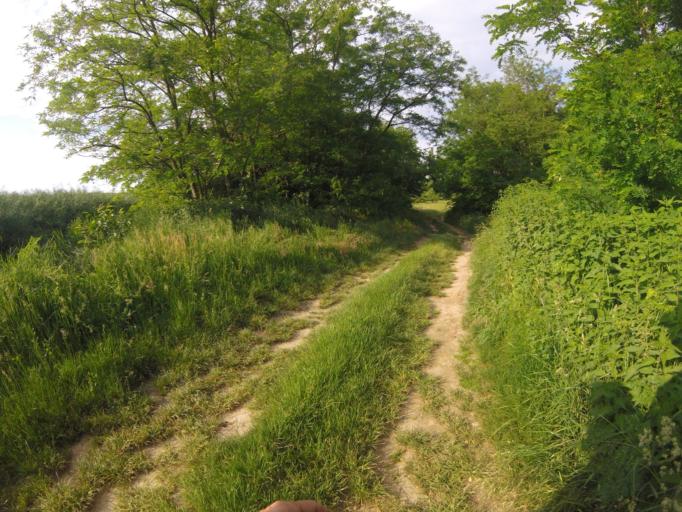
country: HU
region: Zala
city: Zalaszentgrot
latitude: 46.8782
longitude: 17.1235
